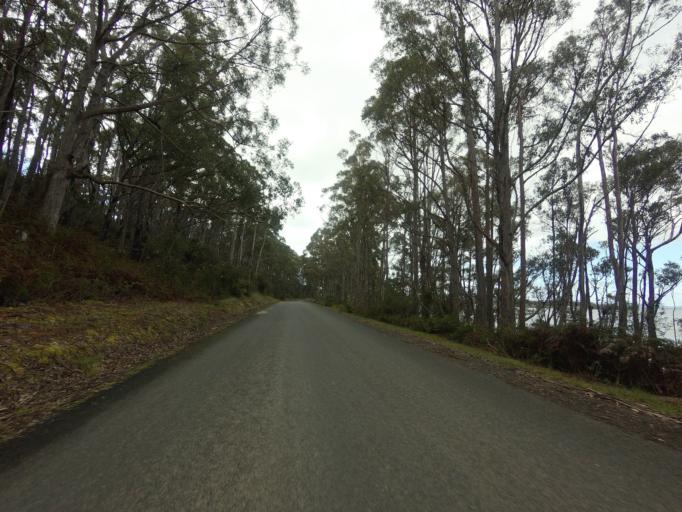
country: AU
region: Tasmania
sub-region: Huon Valley
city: Geeveston
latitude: -43.4357
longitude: 146.9641
